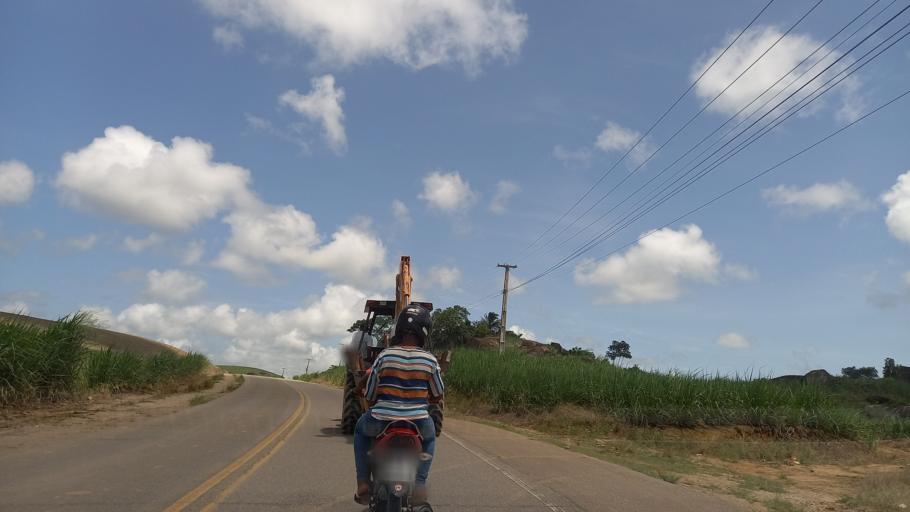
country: BR
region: Pernambuco
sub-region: Sirinhaem
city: Sirinhaem
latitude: -8.6029
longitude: -35.1160
